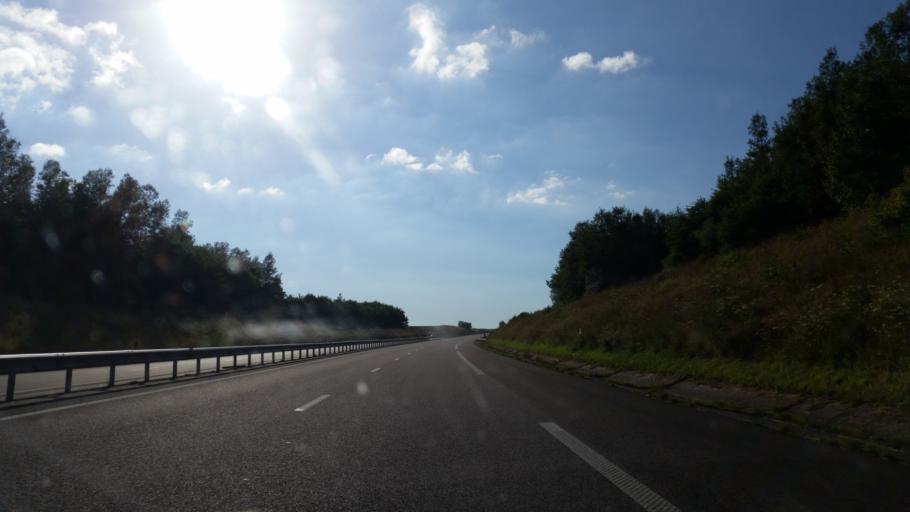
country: FR
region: Haute-Normandie
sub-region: Departement de la Seine-Maritime
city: Cleres
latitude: 49.6314
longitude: 1.1184
